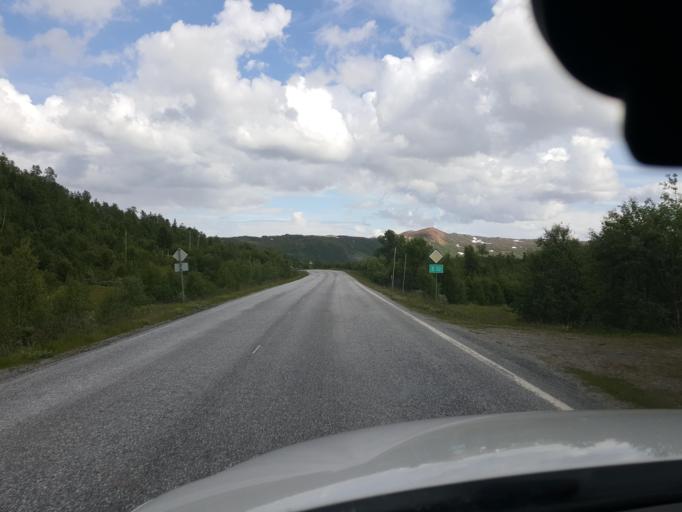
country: NO
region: Nordland
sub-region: Rana
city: Mo i Rana
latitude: 66.2866
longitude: 14.4626
